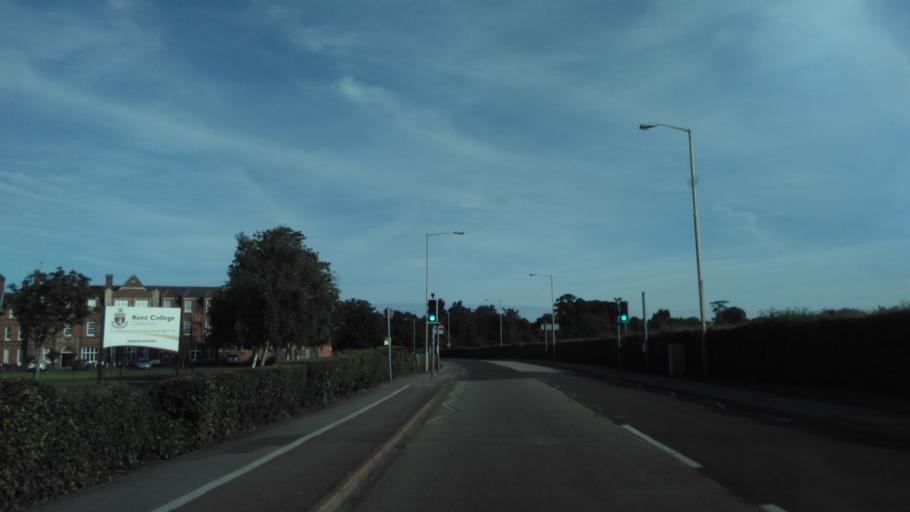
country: GB
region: England
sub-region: Kent
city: Blean
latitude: 51.2930
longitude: 1.0573
